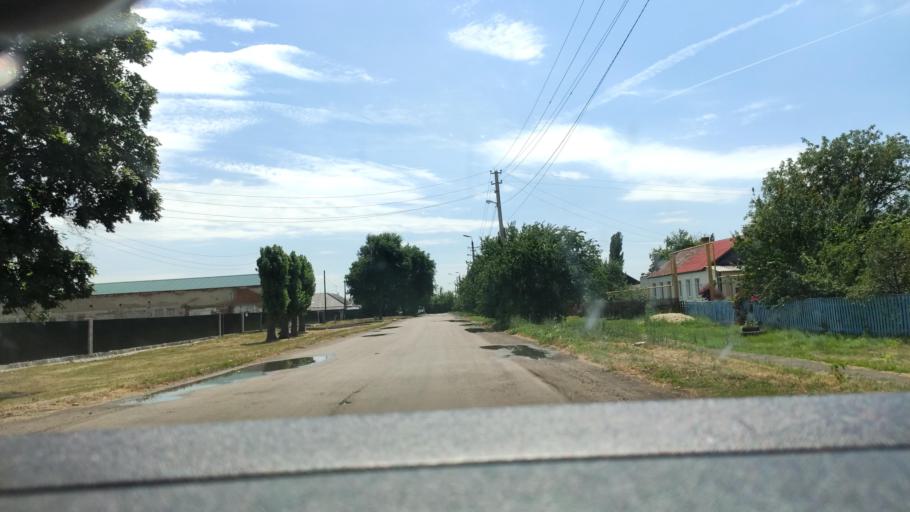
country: RU
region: Voronezj
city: Maslovka
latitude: 51.5080
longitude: 39.2939
